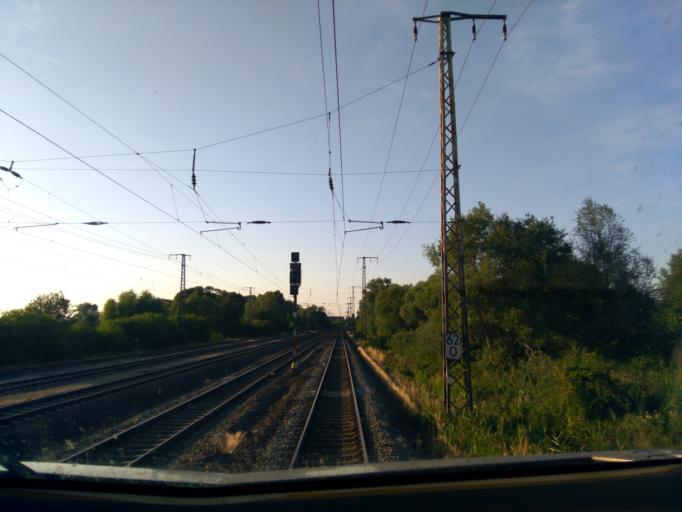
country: DE
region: Mecklenburg-Vorpommern
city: Feldstadt
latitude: 53.5995
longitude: 11.3846
